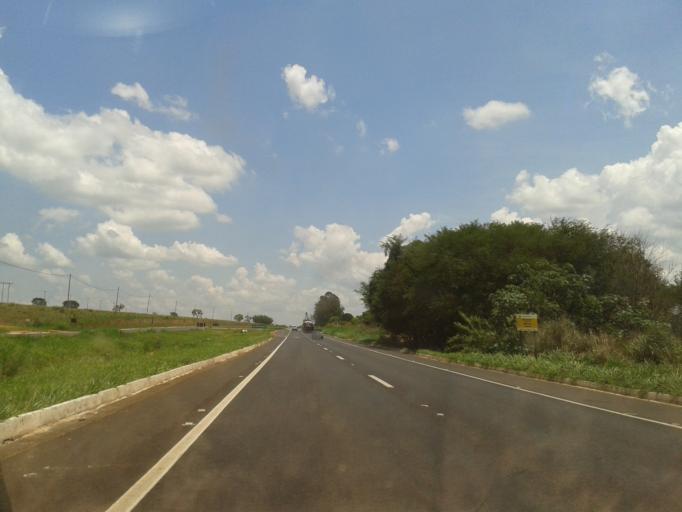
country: BR
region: Minas Gerais
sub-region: Uberlandia
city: Uberlandia
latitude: -18.8892
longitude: -48.4410
